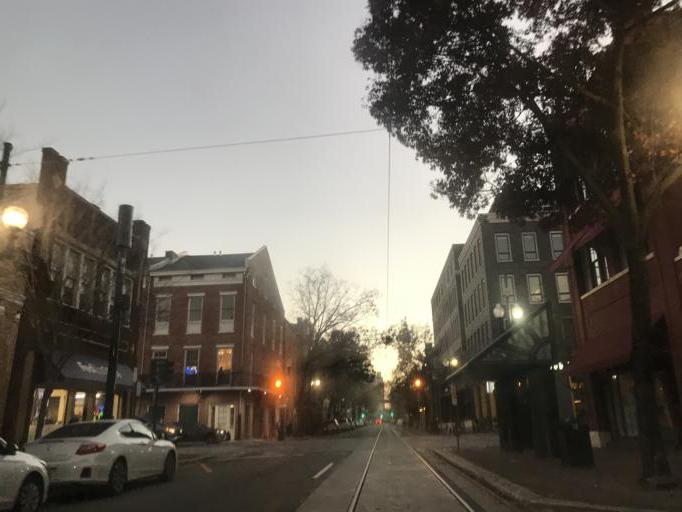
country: US
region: Louisiana
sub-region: Orleans Parish
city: New Orleans
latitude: 29.9463
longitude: -90.0716
